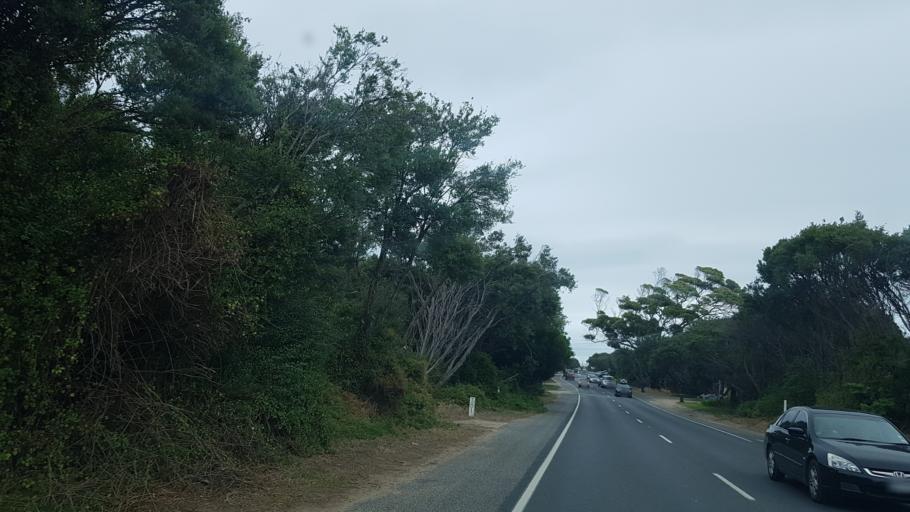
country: AU
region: Victoria
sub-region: Mornington Peninsula
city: Blairgowrie
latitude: -38.3700
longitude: 144.7733
